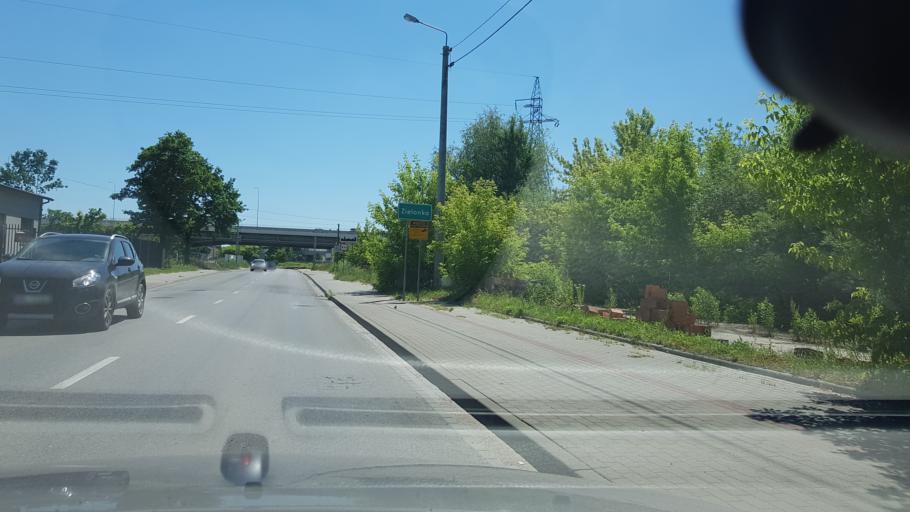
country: PL
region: Masovian Voivodeship
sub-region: Powiat wolominski
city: Marki
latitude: 52.3138
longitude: 21.1237
